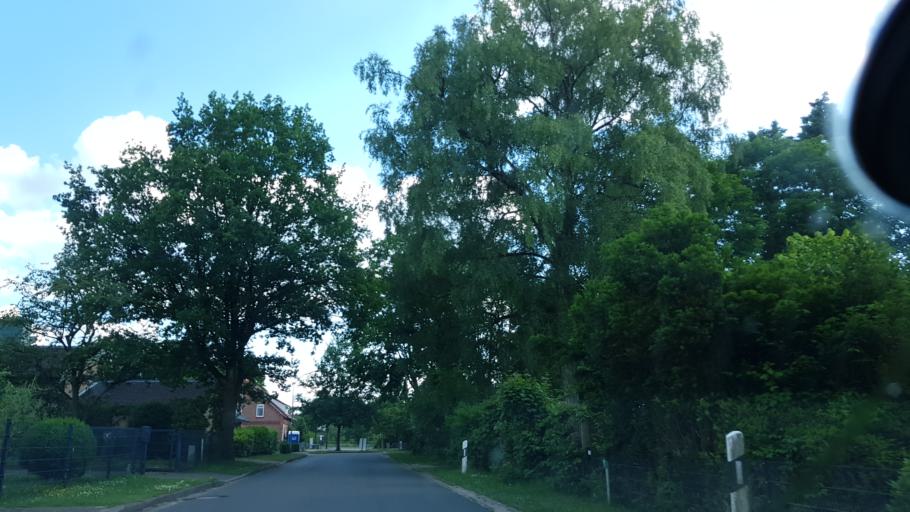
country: DE
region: Lower Saxony
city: Wenzendorf
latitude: 53.3527
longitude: 9.7693
